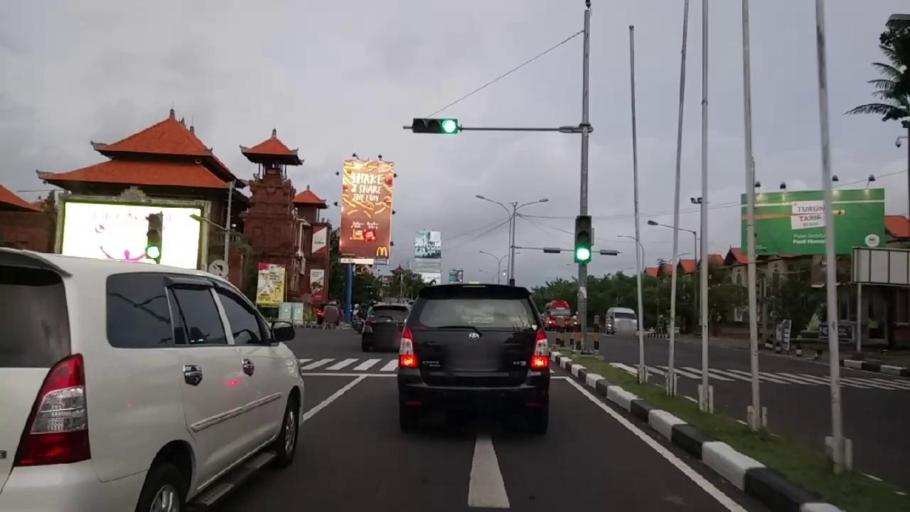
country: ID
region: Bali
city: Kelanabian
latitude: -8.7446
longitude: 115.1787
